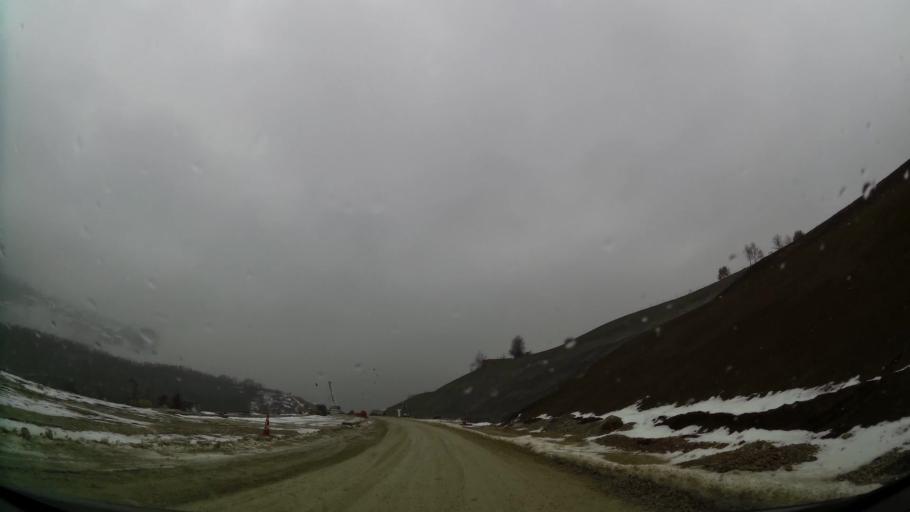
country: XK
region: Ferizaj
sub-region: Hani i Elezit
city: Hani i Elezit
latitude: 42.1655
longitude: 21.2839
